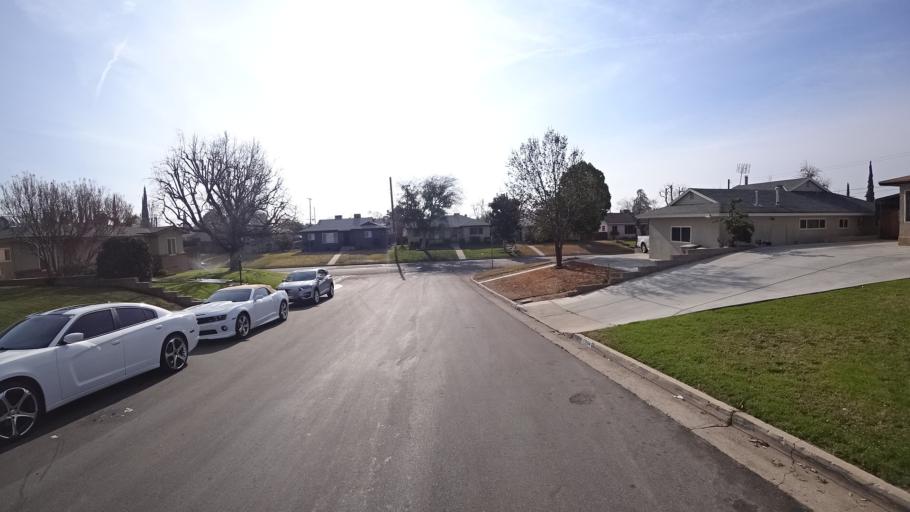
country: US
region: California
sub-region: Kern County
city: Oildale
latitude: 35.4033
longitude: -118.9790
